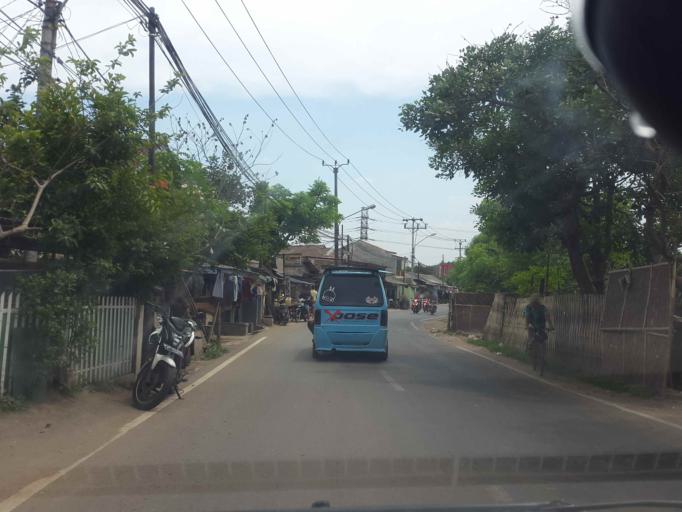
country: ID
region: Banten
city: Tangerang
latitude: -6.1573
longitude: 106.6305
